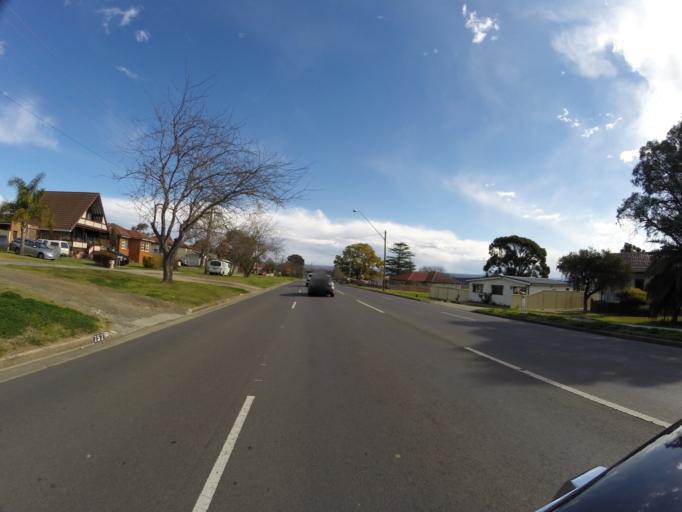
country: AU
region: New South Wales
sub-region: Camden
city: Narellan
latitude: -34.0428
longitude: 150.7287
